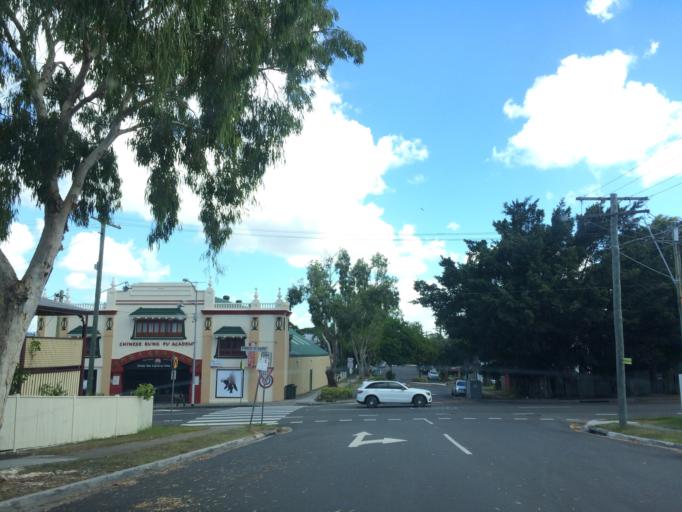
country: AU
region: Queensland
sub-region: Brisbane
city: Woolloongabba
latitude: -27.4877
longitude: 153.0465
